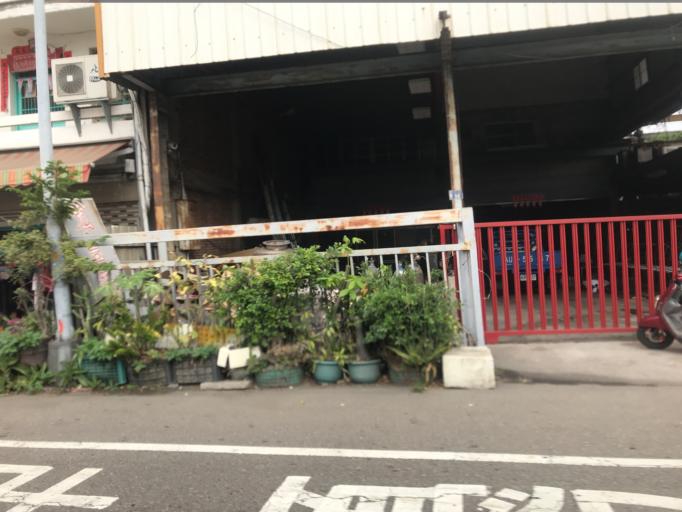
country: TW
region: Taiwan
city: Fengyuan
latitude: 24.3511
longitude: 120.6147
